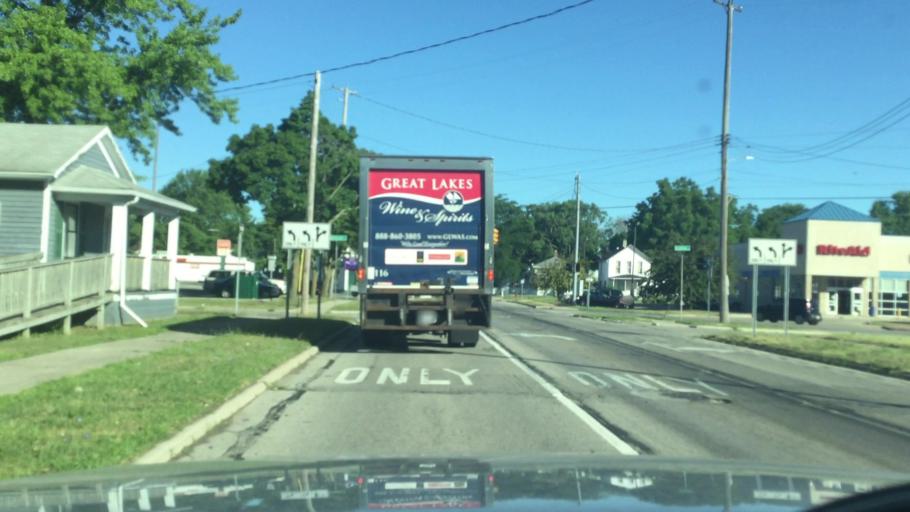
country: US
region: Michigan
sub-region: Saginaw County
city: Saginaw
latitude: 43.4146
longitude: -83.9723
